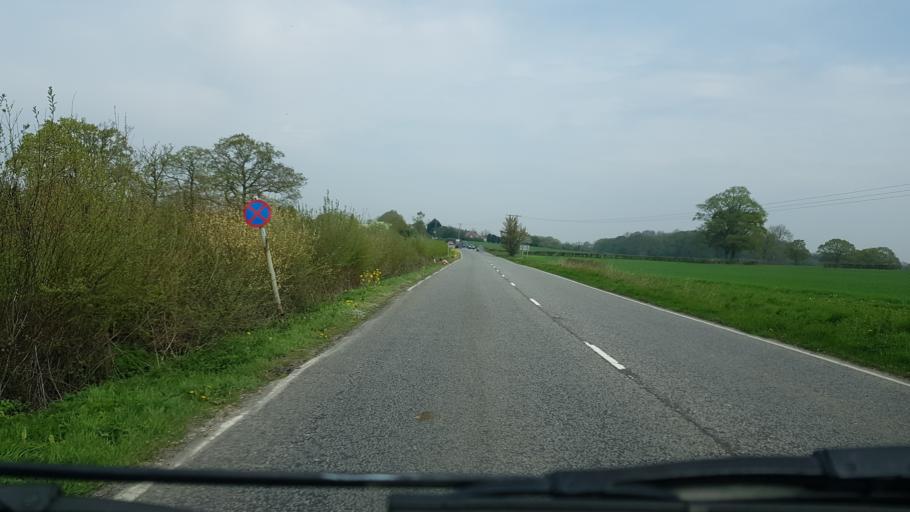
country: GB
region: England
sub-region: Hampshire
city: Kingsclere
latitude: 51.3370
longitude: -1.2589
